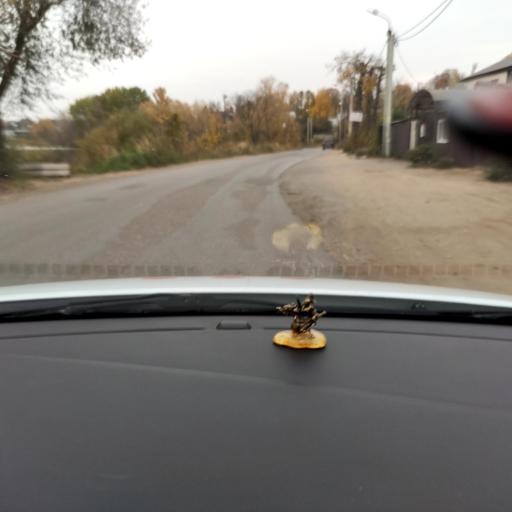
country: RU
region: Tatarstan
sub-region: Gorod Kazan'
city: Kazan
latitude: 55.7253
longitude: 49.1571
